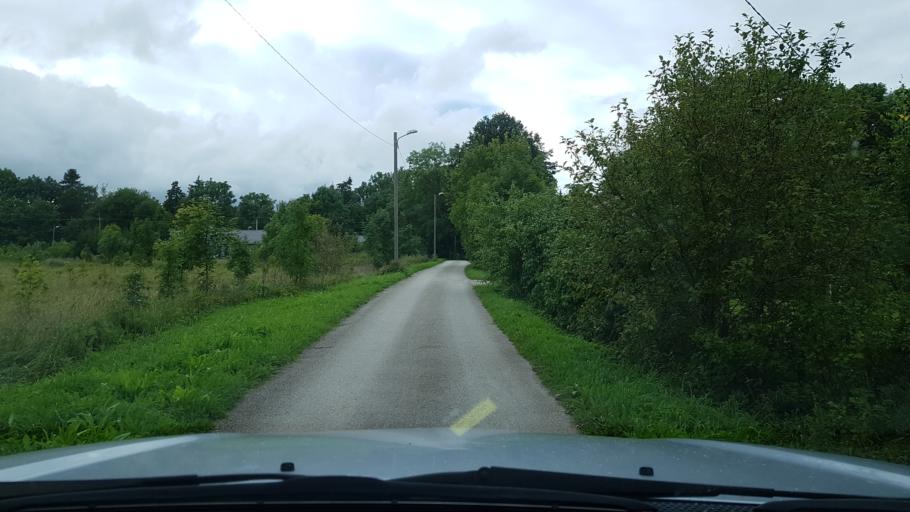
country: EE
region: Harju
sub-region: Rae vald
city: Jueri
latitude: 59.3579
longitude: 24.9523
